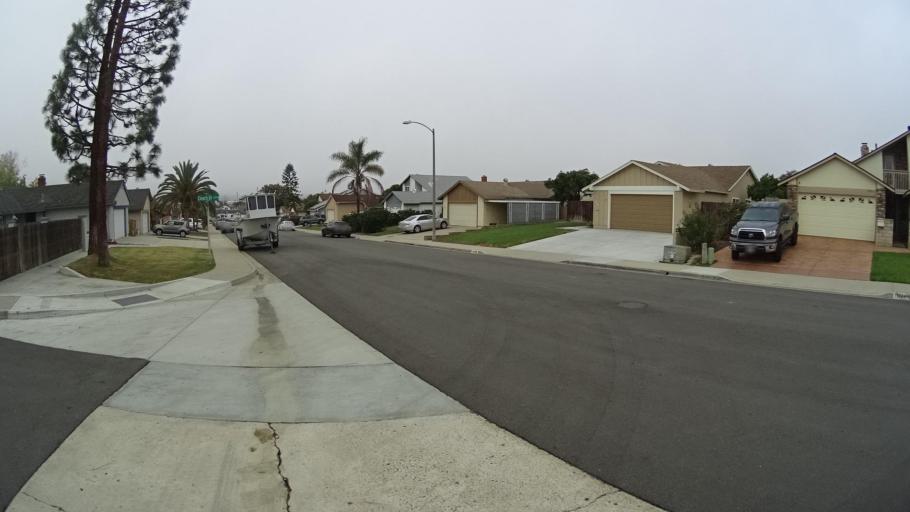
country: US
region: California
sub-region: San Diego County
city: Rancho San Diego
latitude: 32.7310
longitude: -116.9572
